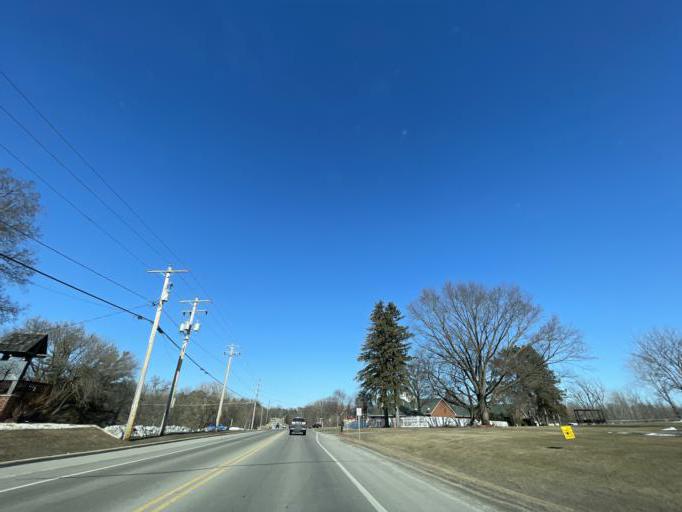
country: US
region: Wisconsin
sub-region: Brown County
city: Suamico
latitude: 44.6298
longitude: -88.0562
